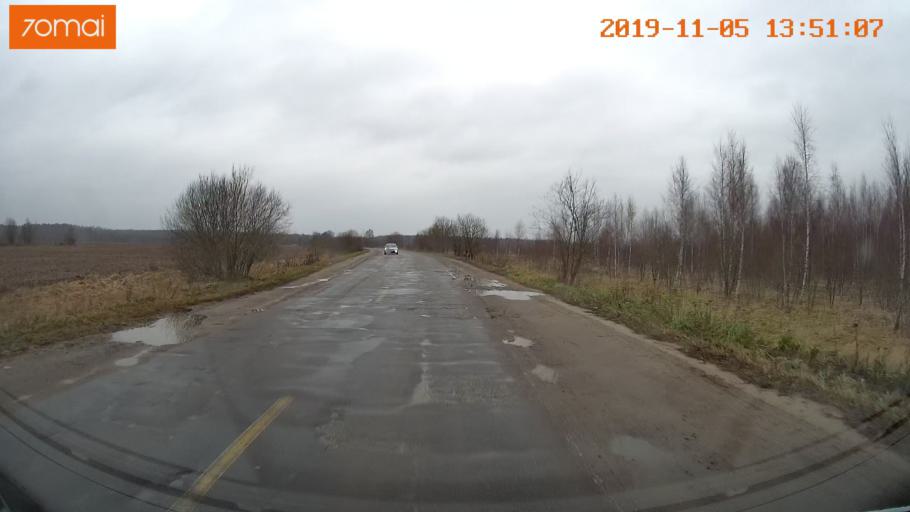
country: RU
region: Ivanovo
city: Kaminskiy
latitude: 57.0236
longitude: 41.4040
